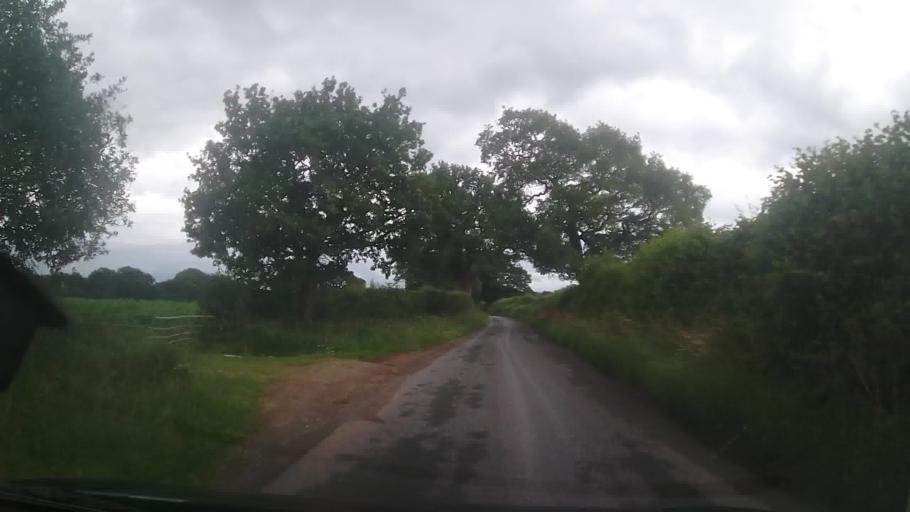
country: GB
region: England
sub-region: Shropshire
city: Whitchurch
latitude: 52.9380
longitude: -2.7299
